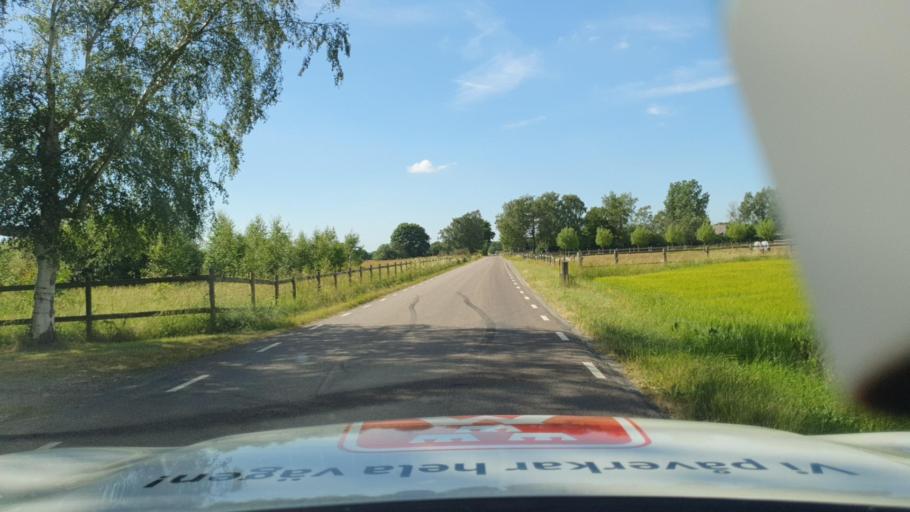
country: SE
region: Skane
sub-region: Sjobo Kommun
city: Blentarp
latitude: 55.6206
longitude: 13.6313
